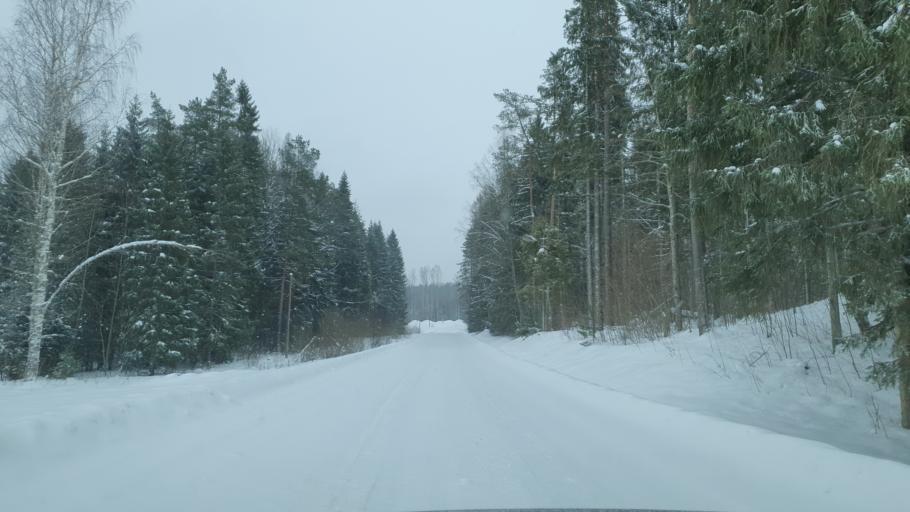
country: EE
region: Tartu
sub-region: Tartu linn
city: Tartu
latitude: 58.5691
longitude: 26.8348
